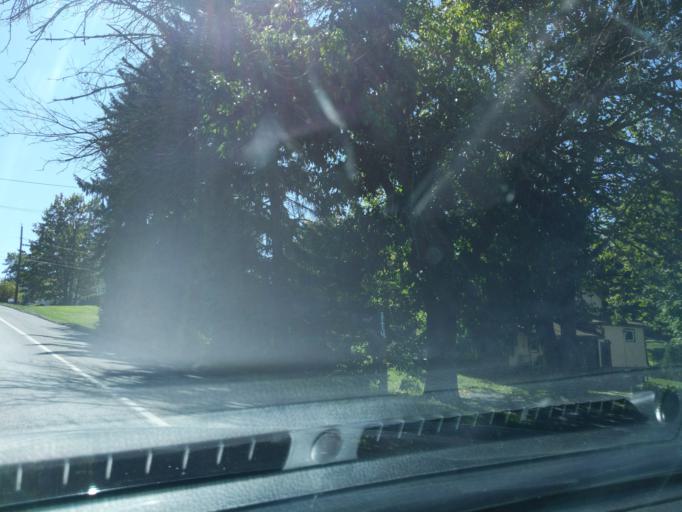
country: US
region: Pennsylvania
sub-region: Blair County
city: Greenwood
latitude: 40.5268
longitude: -78.3645
